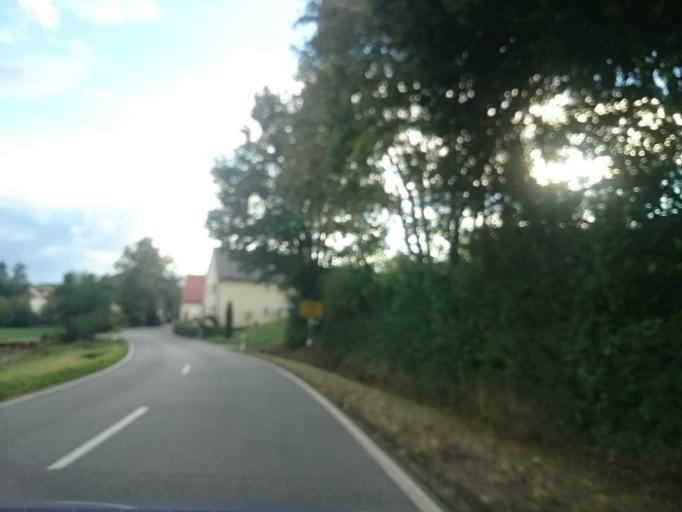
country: DE
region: Bavaria
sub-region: Regierungsbezirk Mittelfranken
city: Thalmassing
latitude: 49.1256
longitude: 11.1935
